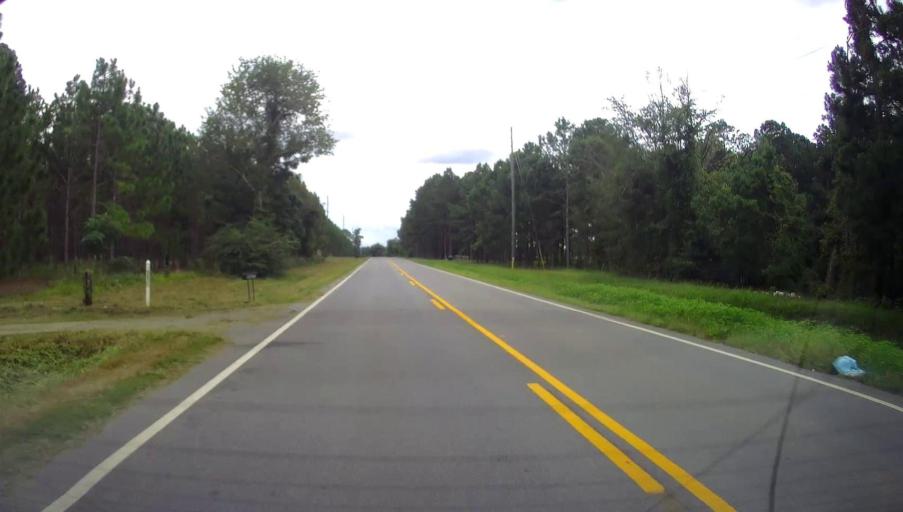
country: US
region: Georgia
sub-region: Macon County
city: Oglethorpe
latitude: 32.2662
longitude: -84.1050
